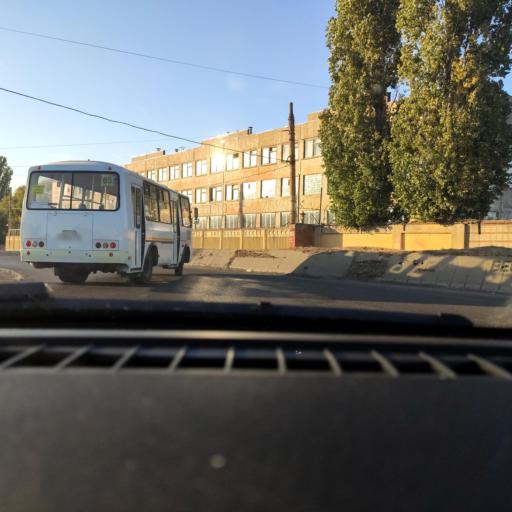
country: RU
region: Voronezj
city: Maslovka
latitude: 51.5992
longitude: 39.2497
